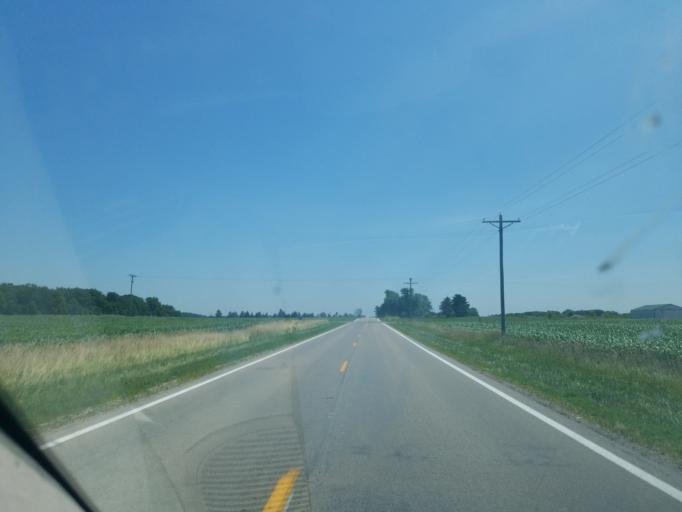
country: US
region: Ohio
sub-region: Mercer County
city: Rockford
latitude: 40.7423
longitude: -84.6904
